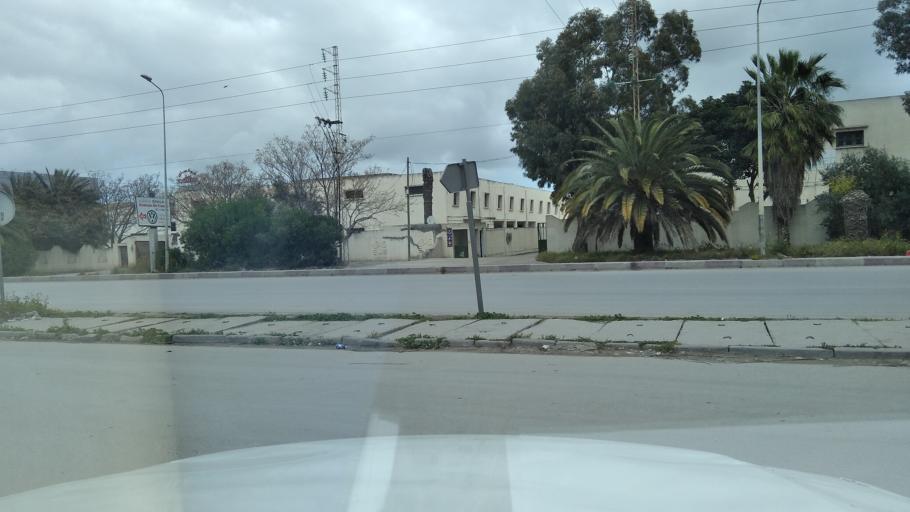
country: TN
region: Bin 'Arus
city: Ben Arous
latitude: 36.7631
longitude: 10.2284
